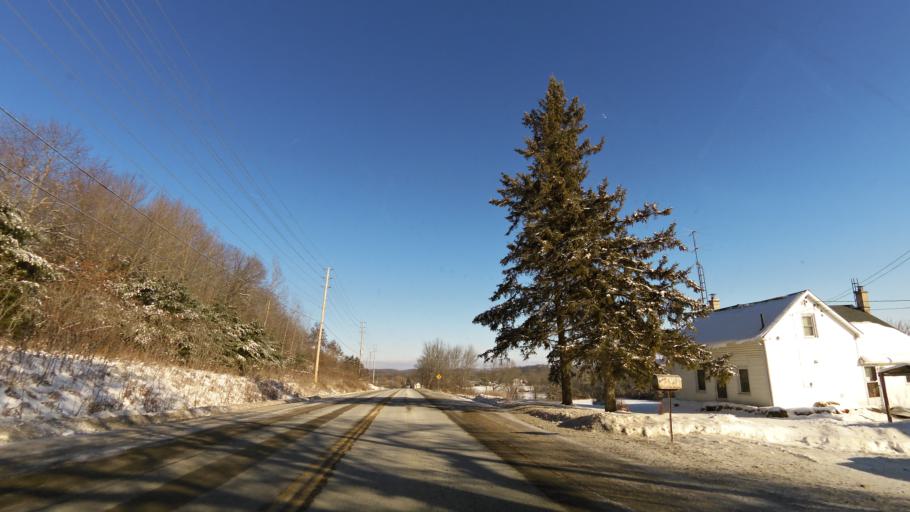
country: CA
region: Ontario
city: Quinte West
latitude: 44.2419
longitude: -77.8182
